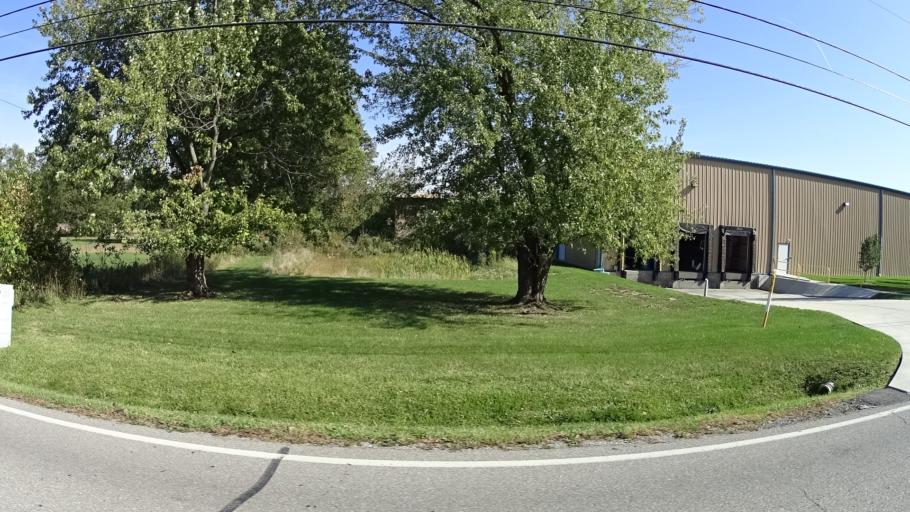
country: US
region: Ohio
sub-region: Lorain County
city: Vermilion-on-the-Lake
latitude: 41.4141
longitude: -82.3044
